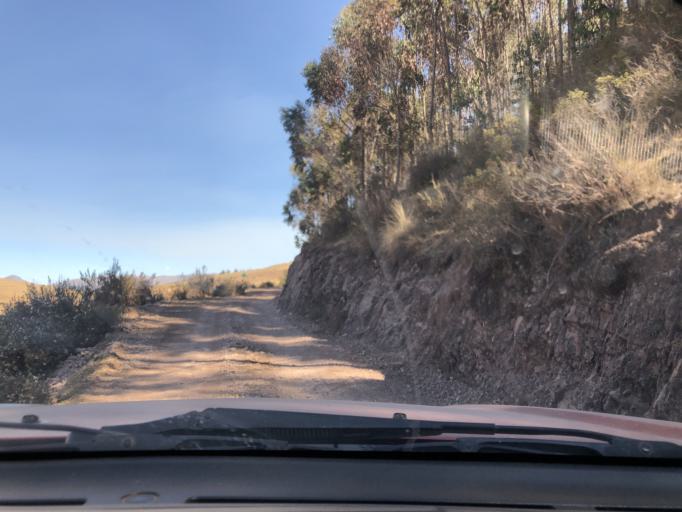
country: PE
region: Ayacucho
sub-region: Provincia de La Mar
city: Chilcas
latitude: -13.1833
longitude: -73.8410
